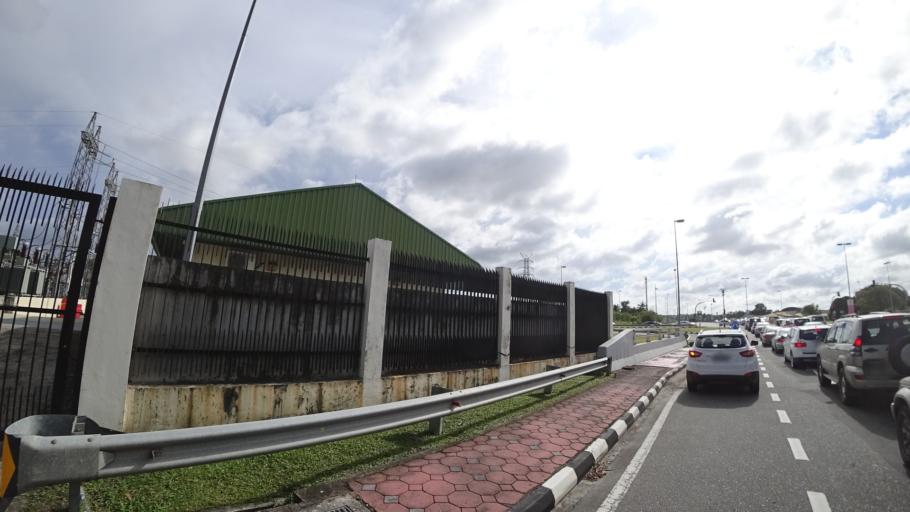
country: BN
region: Brunei and Muara
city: Bandar Seri Begawan
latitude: 4.9089
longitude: 114.9096
